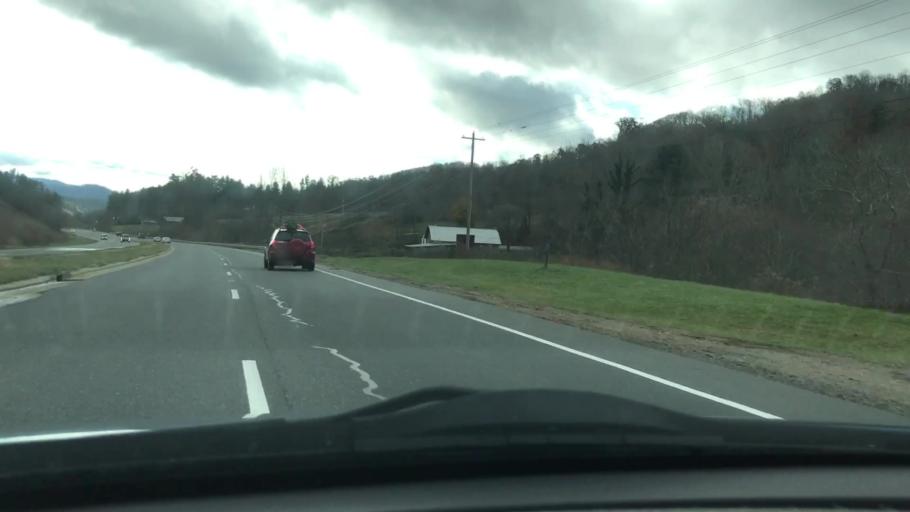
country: US
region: North Carolina
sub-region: Madison County
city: Mars Hill
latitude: 35.8902
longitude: -82.4761
